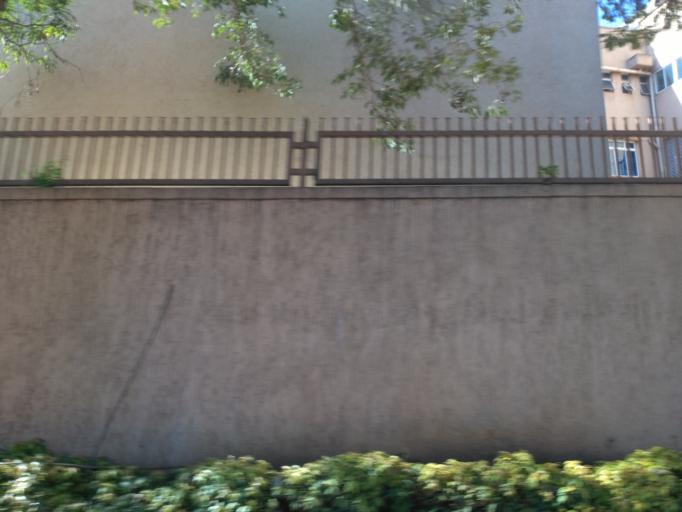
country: UG
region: Central Region
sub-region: Kampala District
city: Kampala
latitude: 0.3150
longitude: 32.5917
